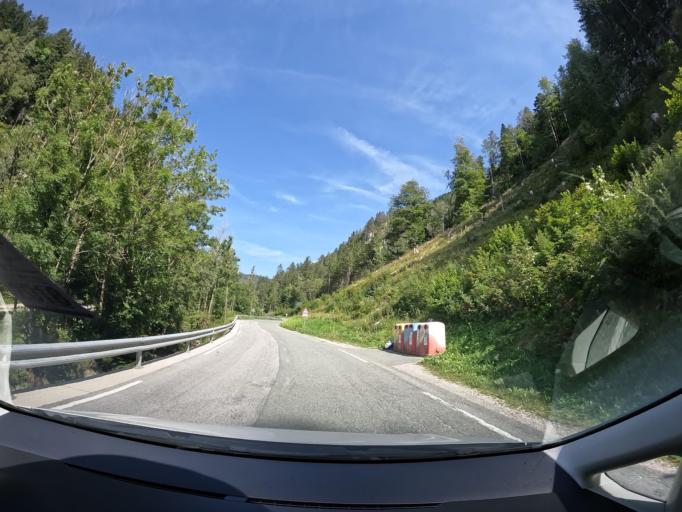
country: SI
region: Jesenice
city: Koroska Bela
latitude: 46.4728
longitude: 14.1045
